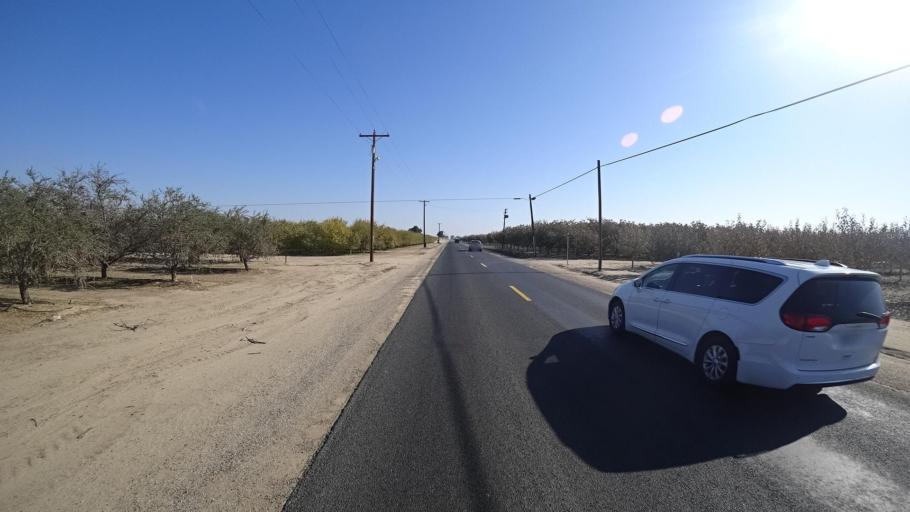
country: US
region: California
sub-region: Kern County
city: Delano
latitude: 35.7177
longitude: -119.3485
